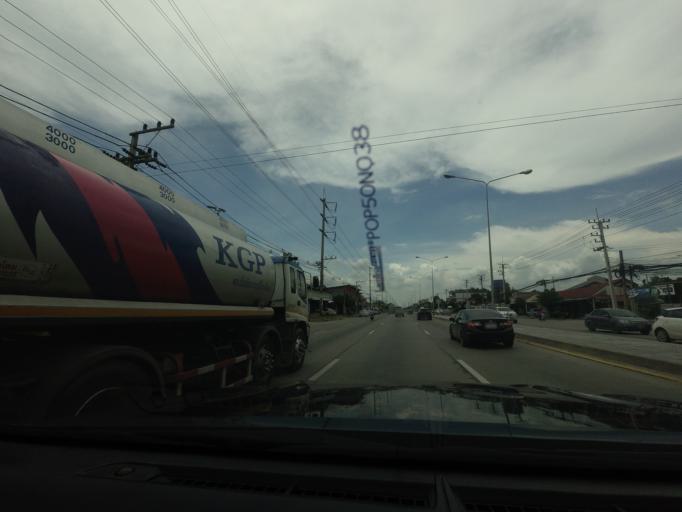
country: TH
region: Nakhon Pathom
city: Nakhon Pathom
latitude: 13.8422
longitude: 100.0267
